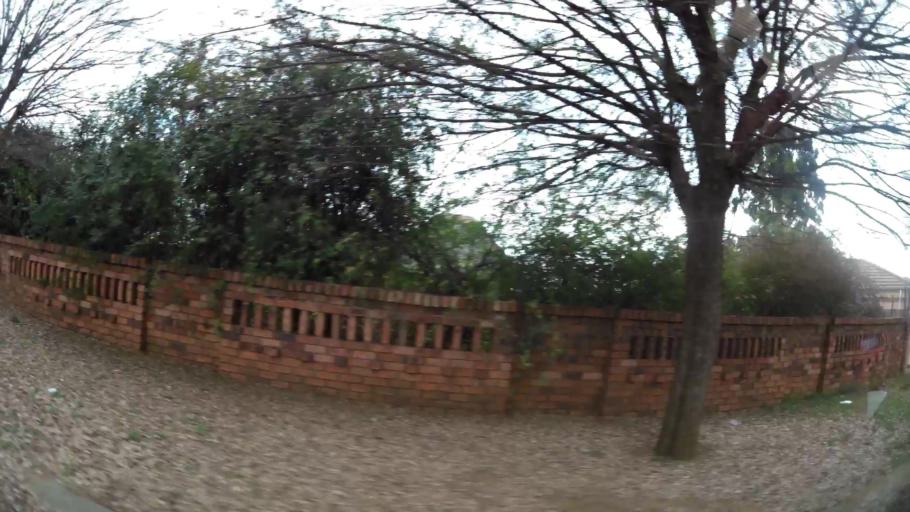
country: ZA
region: Gauteng
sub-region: Ekurhuleni Metropolitan Municipality
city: Benoni
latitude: -26.1353
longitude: 28.3599
